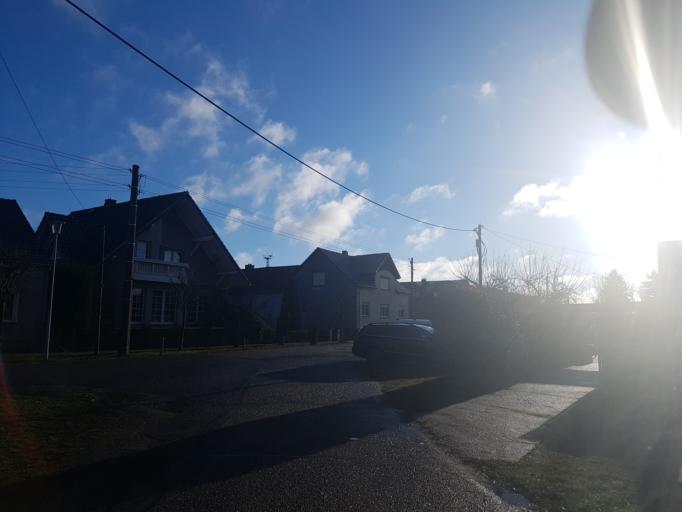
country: DE
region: Brandenburg
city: Bad Liebenwerda
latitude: 51.4928
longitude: 13.3337
